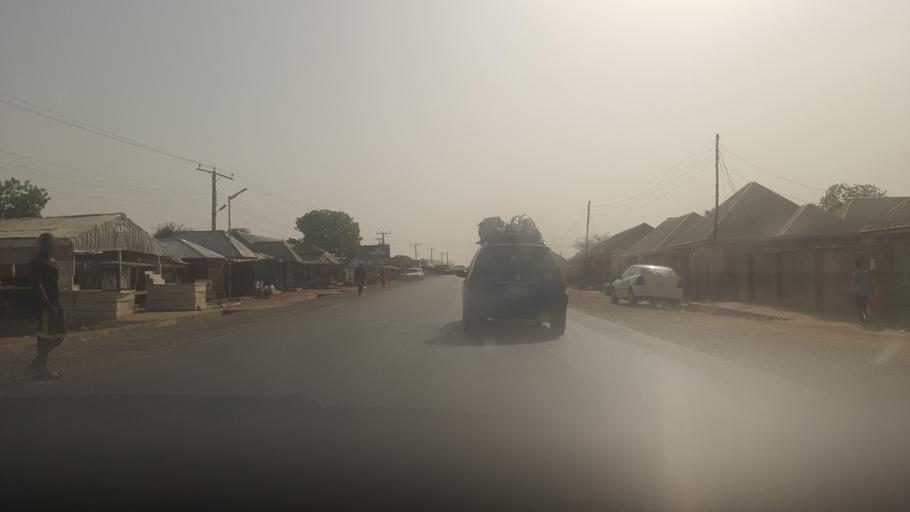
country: NG
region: Bauchi
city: Dindima
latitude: 10.2618
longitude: 9.9975
